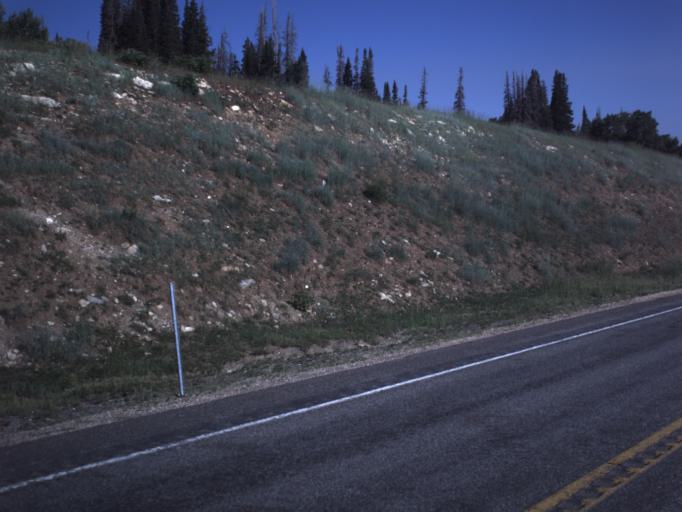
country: US
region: Utah
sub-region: Sanpete County
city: Fairview
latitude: 39.6408
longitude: -111.3300
